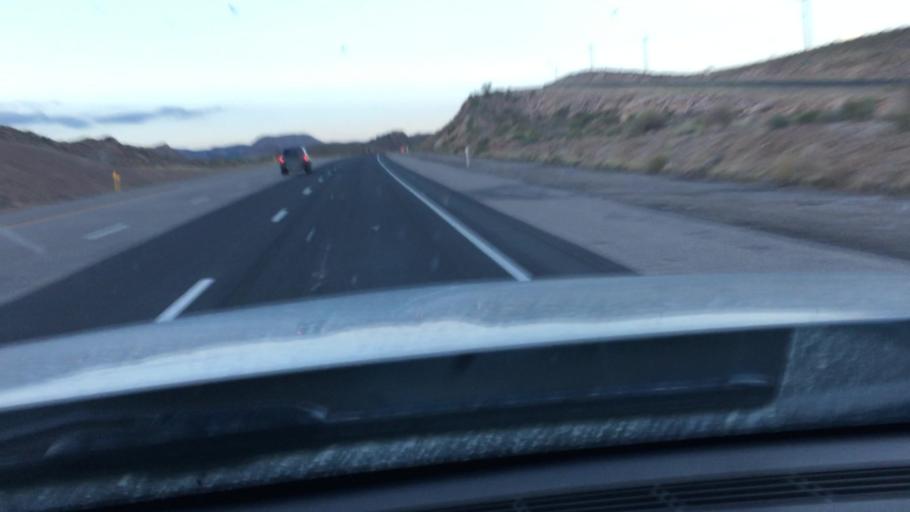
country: US
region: Utah
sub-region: Washington County
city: Hurricane
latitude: 37.2141
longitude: -113.3901
